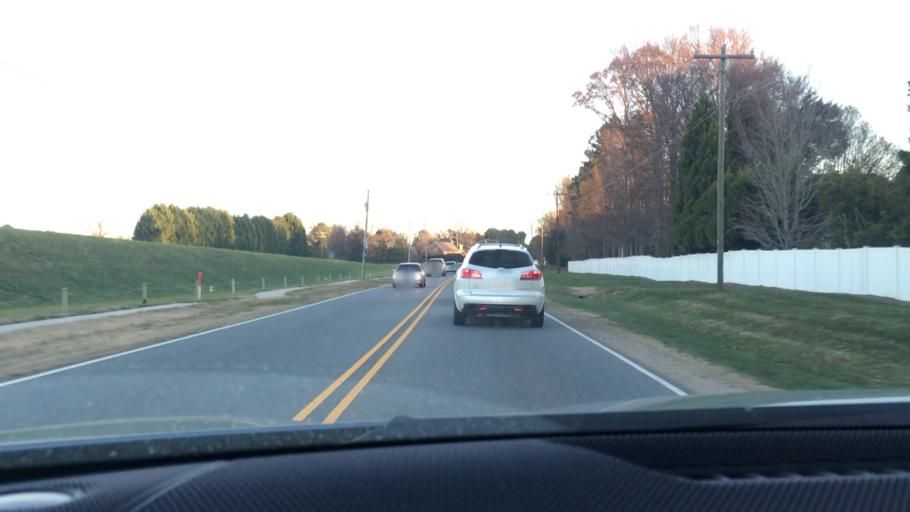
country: US
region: North Carolina
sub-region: Mecklenburg County
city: Cornelius
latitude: 35.4380
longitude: -80.9025
